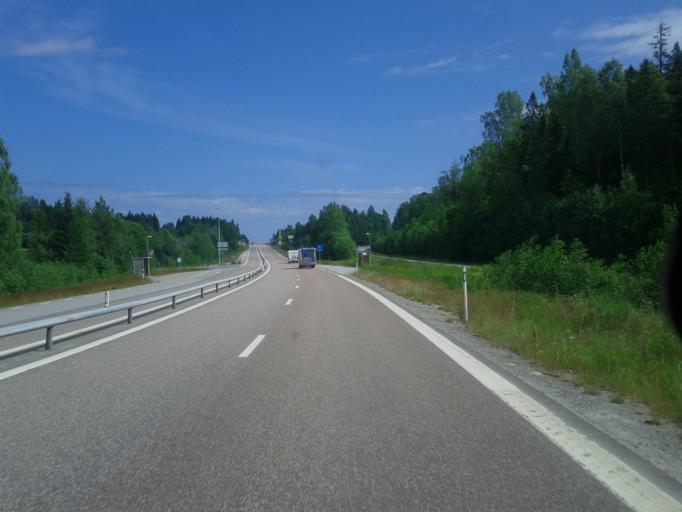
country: SE
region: Vaesternorrland
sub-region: OErnskoeldsviks Kommun
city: Husum
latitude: 63.3474
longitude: 19.1412
